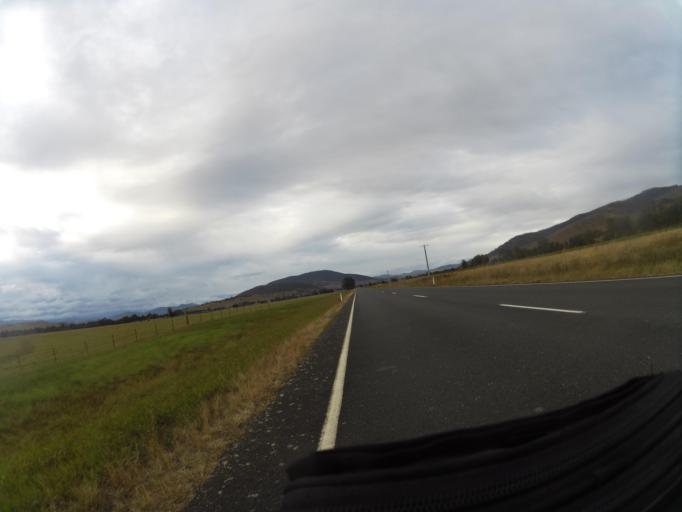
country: AU
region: New South Wales
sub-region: Snowy River
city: Jindabyne
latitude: -36.0981
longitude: 147.9816
